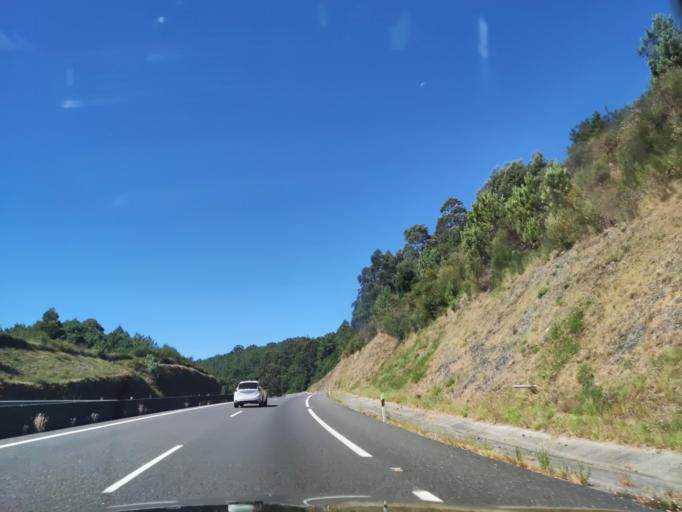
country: ES
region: Galicia
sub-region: Provincia da Coruna
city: Boiro
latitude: 42.6457
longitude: -8.9063
